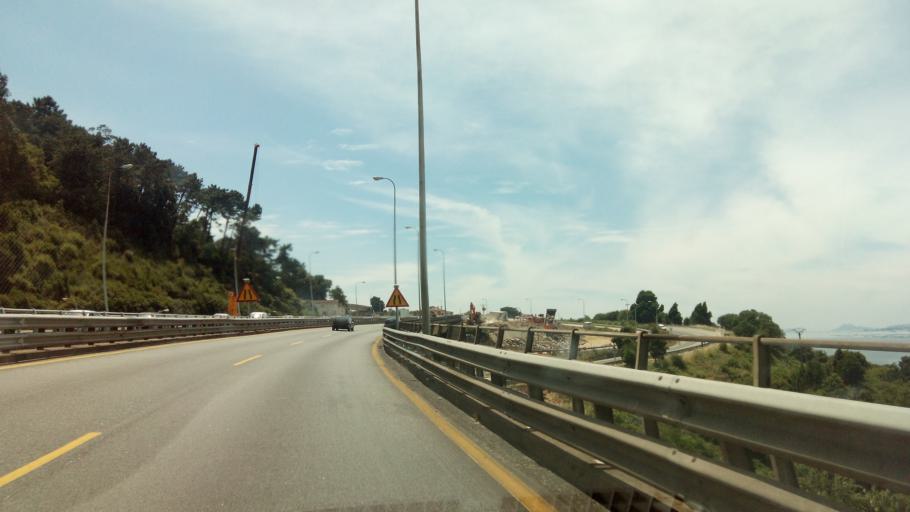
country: ES
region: Galicia
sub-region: Provincia de Pontevedra
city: Redondela
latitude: 42.2802
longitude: -8.6621
